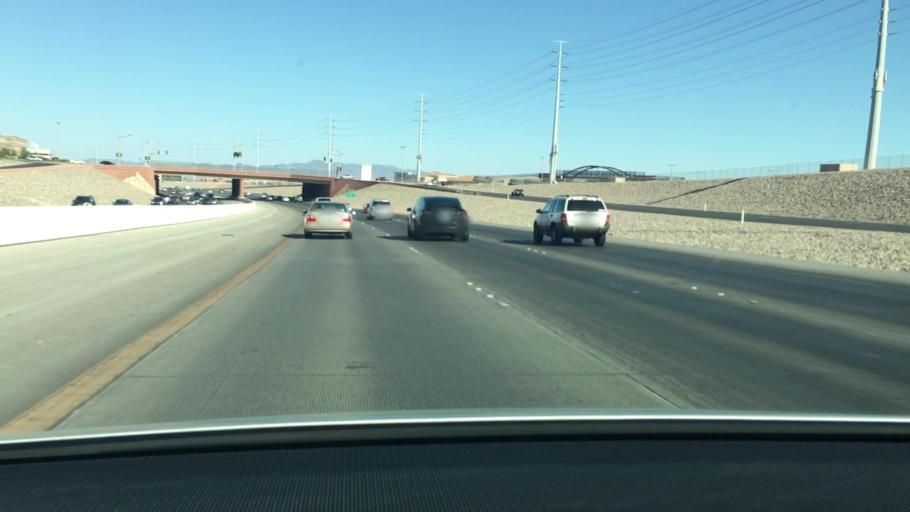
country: US
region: Nevada
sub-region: Clark County
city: Summerlin South
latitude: 36.1233
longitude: -115.3294
